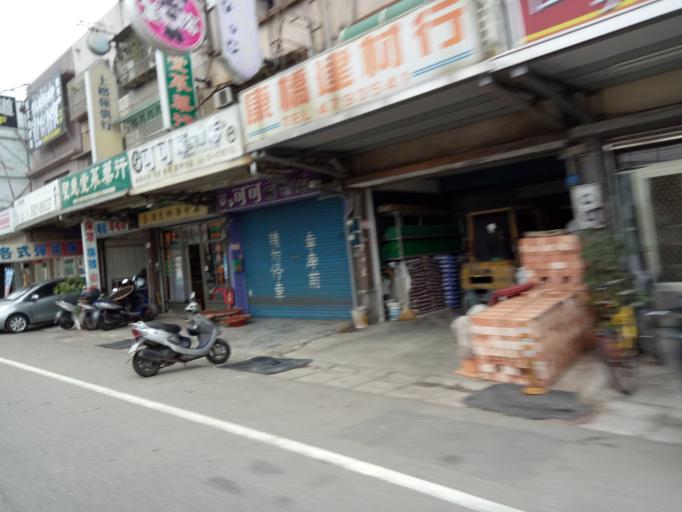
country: TW
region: Taiwan
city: Daxi
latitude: 24.8734
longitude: 121.2315
